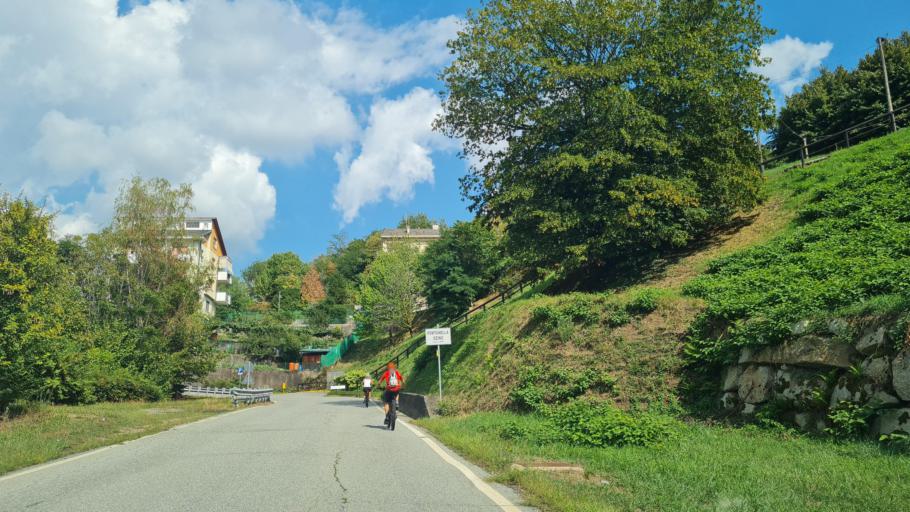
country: IT
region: Piedmont
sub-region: Provincia di Biella
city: Fontanella-Ozino
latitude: 45.6185
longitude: 8.1684
